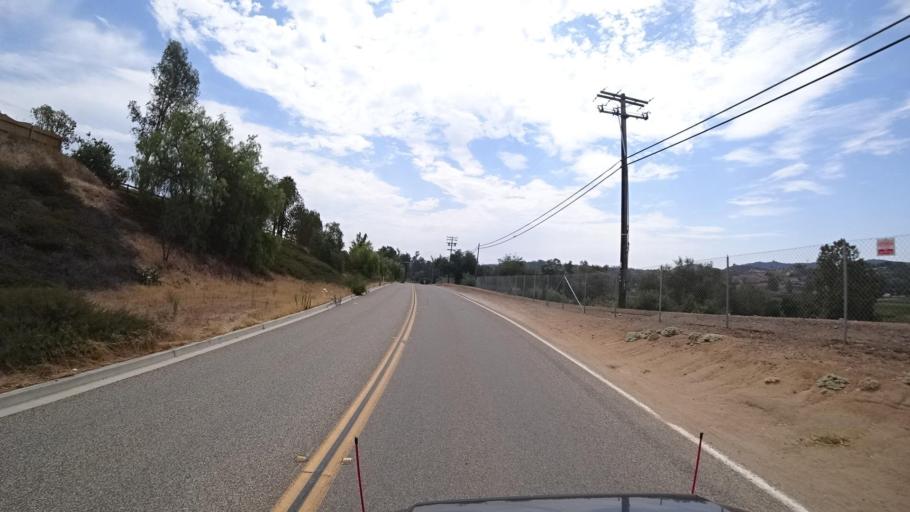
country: US
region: California
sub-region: San Diego County
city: Hidden Meadows
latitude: 33.1851
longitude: -117.0925
